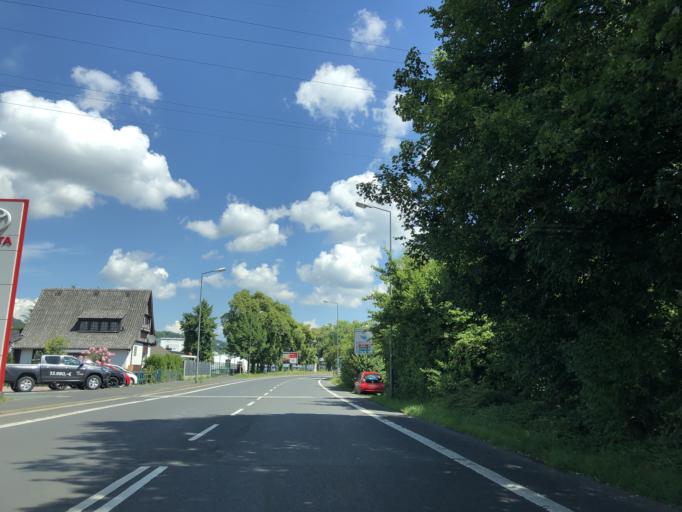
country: DE
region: Hesse
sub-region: Regierungsbezirk Giessen
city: Marburg an der Lahn
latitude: 50.7919
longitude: 8.7528
